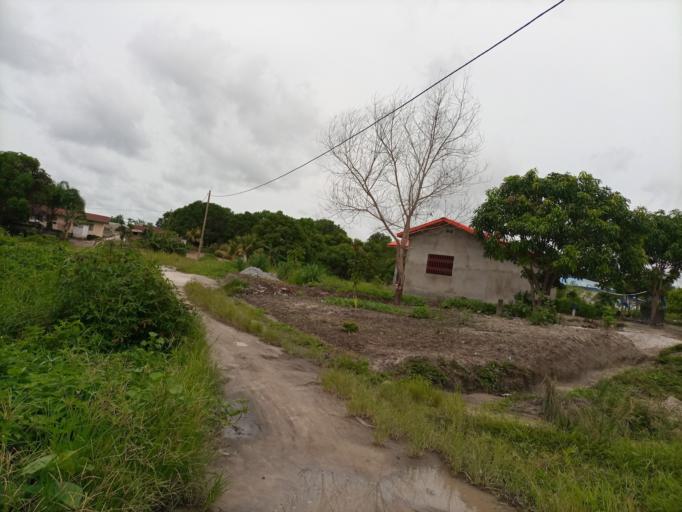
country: SL
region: Southern Province
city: Bo
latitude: 7.9421
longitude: -11.7455
